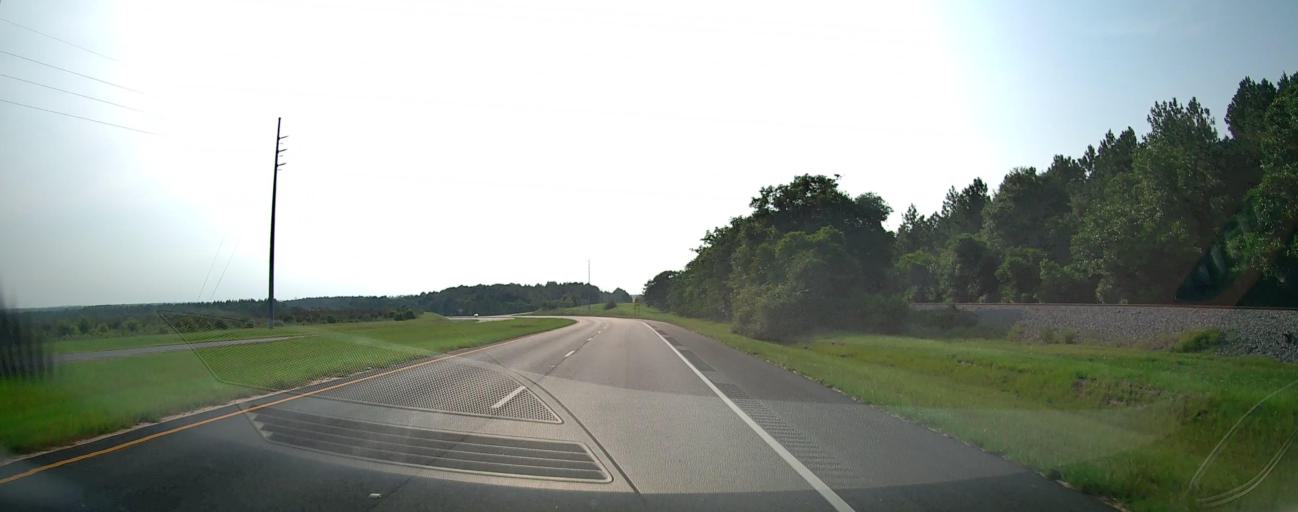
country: US
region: Georgia
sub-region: Taylor County
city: Butler
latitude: 32.5884
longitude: -84.3524
